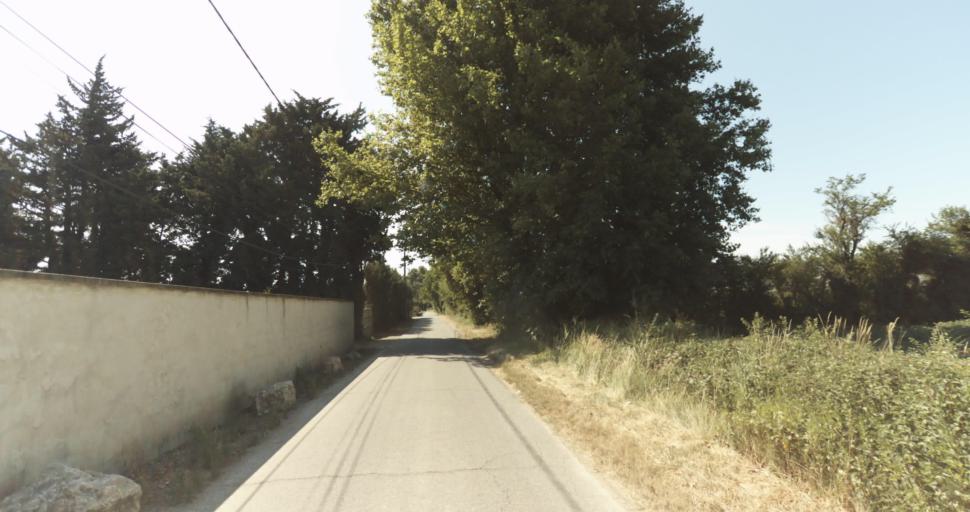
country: FR
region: Provence-Alpes-Cote d'Azur
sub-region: Departement du Vaucluse
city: Althen-des-Paluds
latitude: 44.0127
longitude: 4.9792
